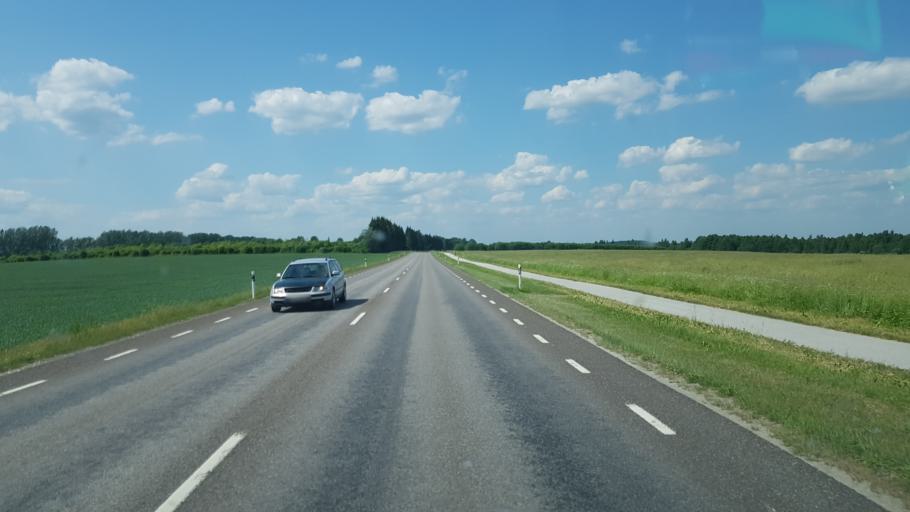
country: EE
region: Jogevamaa
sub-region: Tabivere vald
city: Tabivere
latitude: 58.5405
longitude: 26.6228
